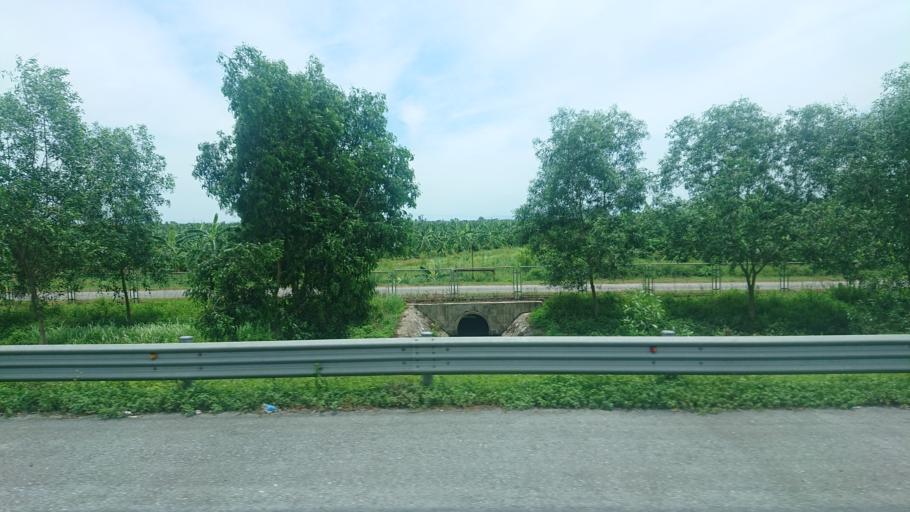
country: VN
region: Hai Phong
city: An Lao
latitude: 20.8175
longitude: 106.4866
